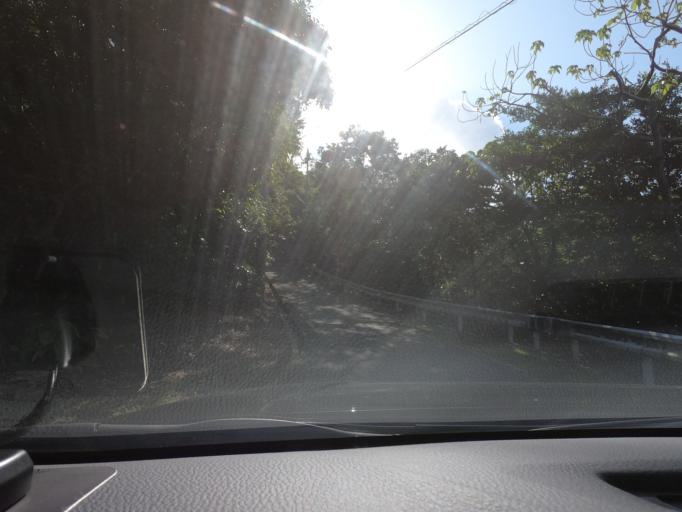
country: JP
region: Okinawa
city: Nago
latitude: 26.7570
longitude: 128.1984
